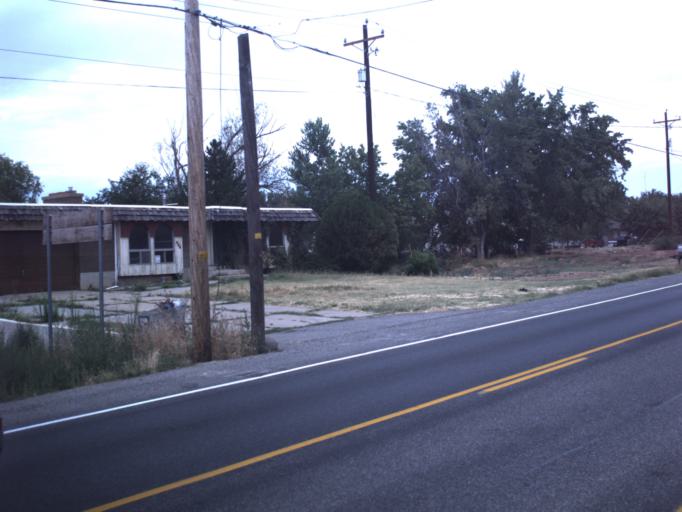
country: US
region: Utah
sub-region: Davis County
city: West Point
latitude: 41.1192
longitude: -112.0645
